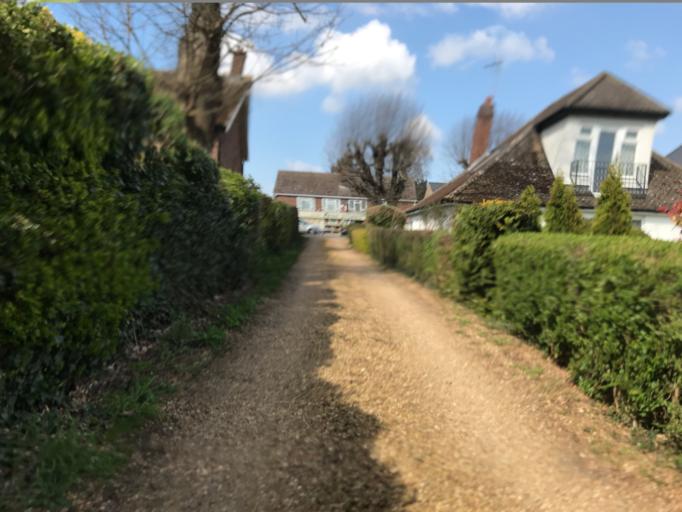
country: GB
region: England
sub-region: Cambridgeshire
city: Sawston
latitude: 52.1504
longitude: 0.1430
